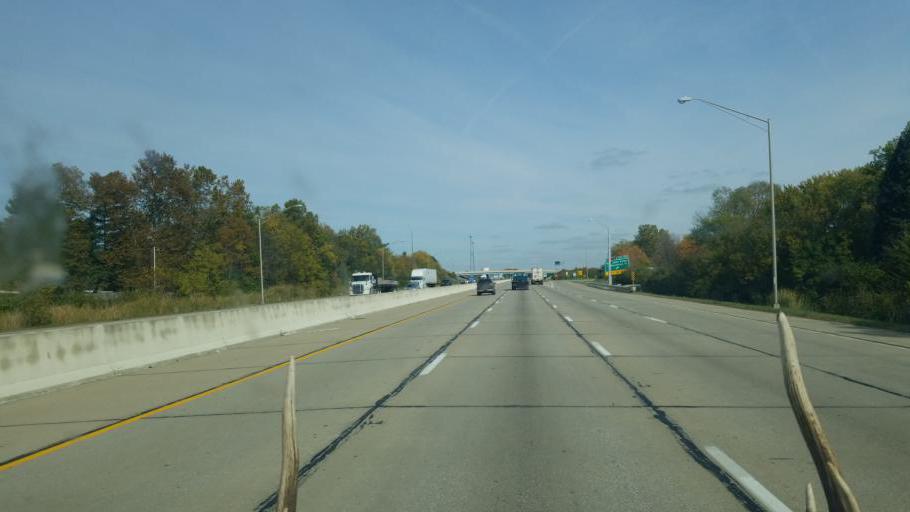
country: US
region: Indiana
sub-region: Marion County
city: Speedway
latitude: 39.7273
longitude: -86.2476
